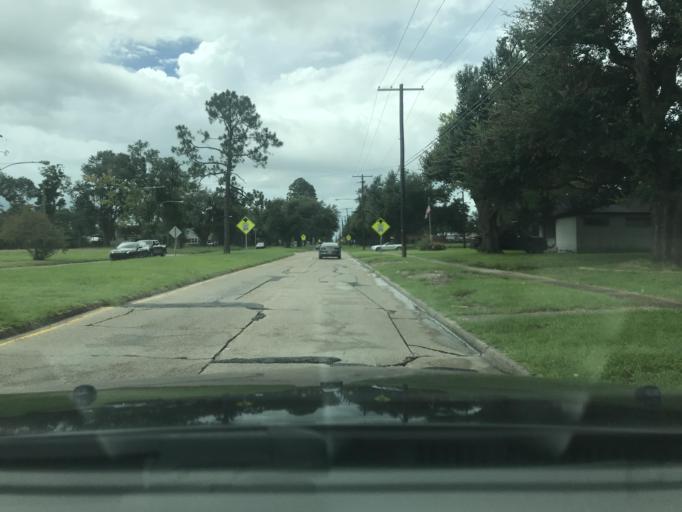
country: US
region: Louisiana
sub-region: Calcasieu Parish
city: Lake Charles
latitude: 30.2100
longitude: -93.2044
